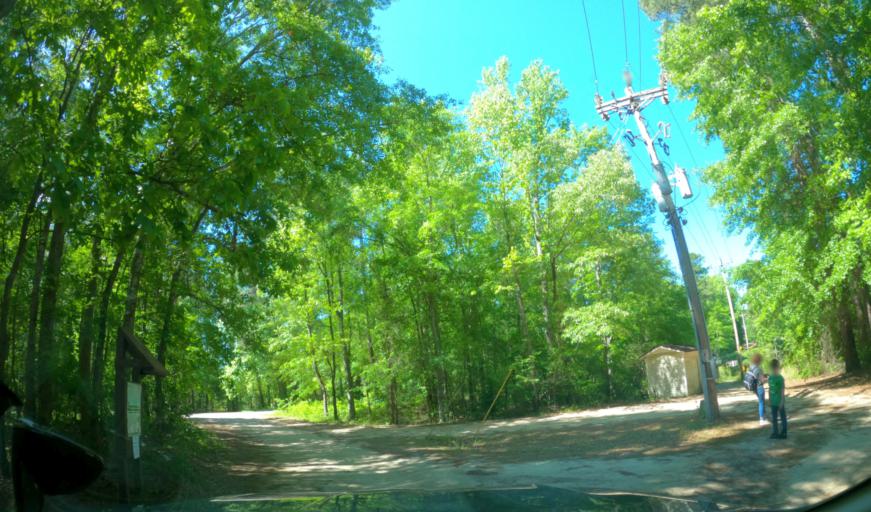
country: US
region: South Carolina
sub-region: Aiken County
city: Gloverville
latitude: 33.4518
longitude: -81.7938
